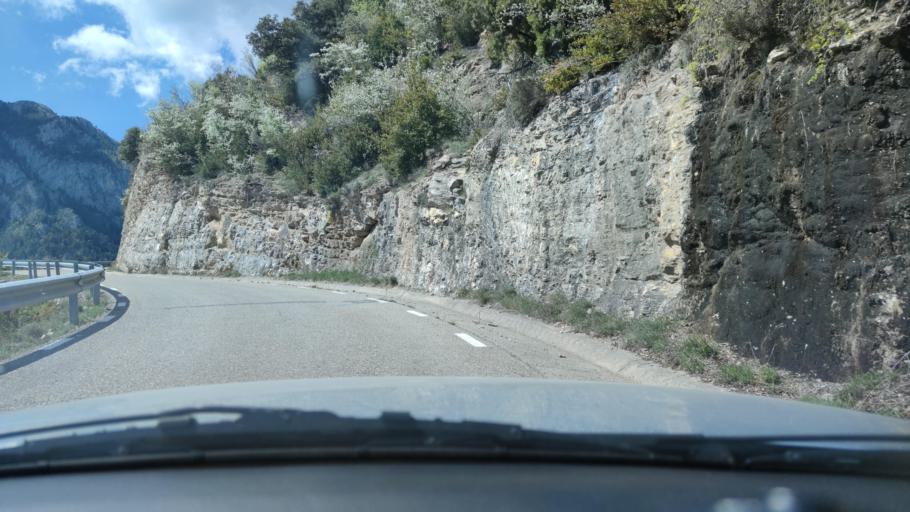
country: ES
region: Catalonia
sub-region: Provincia de Lleida
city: Coll de Nargo
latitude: 42.2914
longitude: 1.2626
